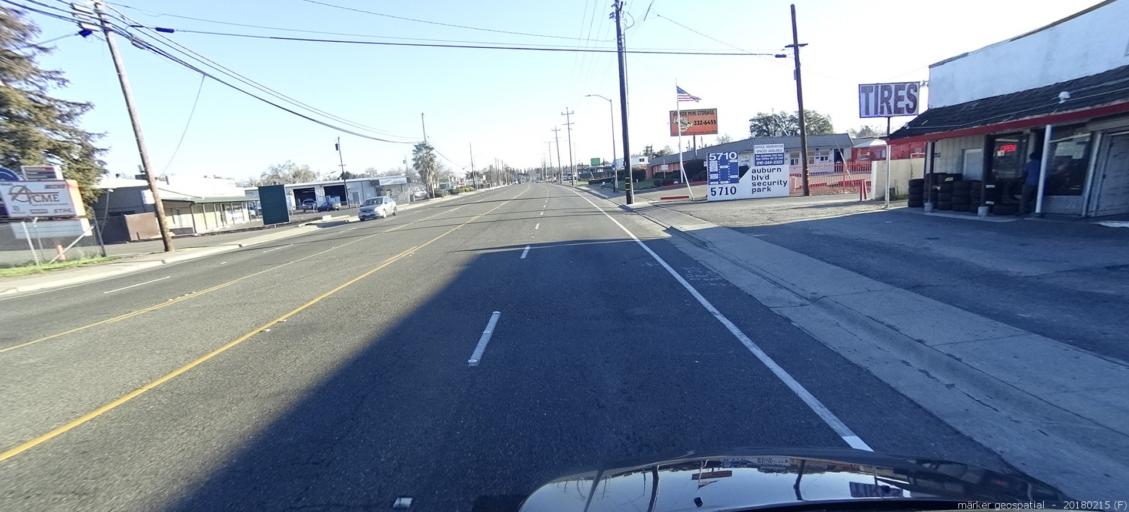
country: US
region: California
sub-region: Sacramento County
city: Foothill Farms
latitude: 38.6702
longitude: -121.3322
